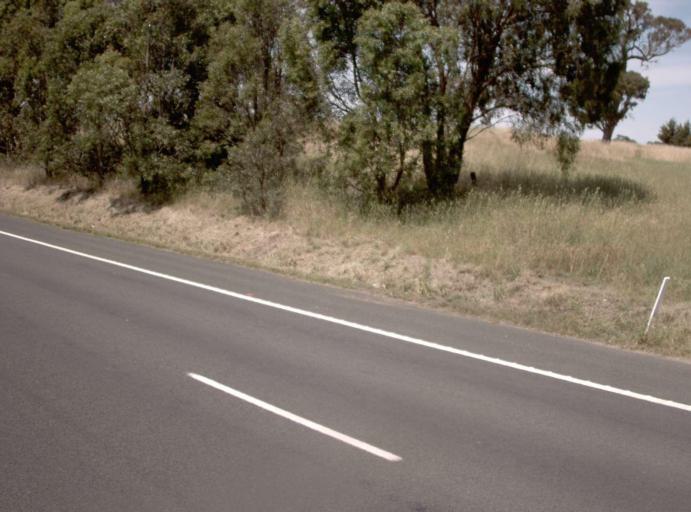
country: AU
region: Victoria
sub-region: Latrobe
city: Traralgon
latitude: -38.1614
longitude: 146.7052
